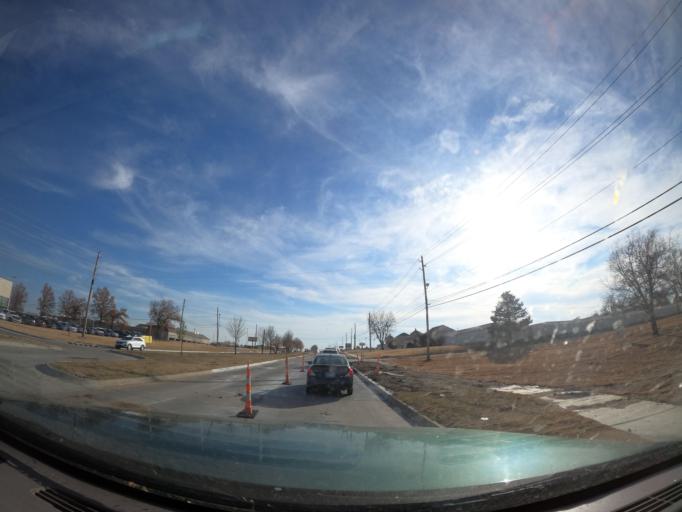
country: US
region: Oklahoma
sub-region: Tulsa County
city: Jenks
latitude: 36.0359
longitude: -95.8864
